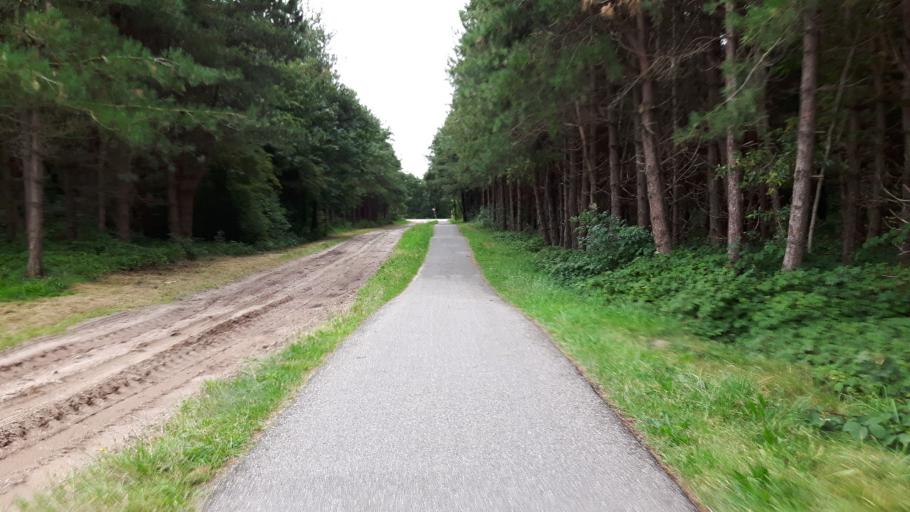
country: NL
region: Friesland
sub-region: Gemeente Ameland
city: Nes
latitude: 53.4474
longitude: 5.7125
